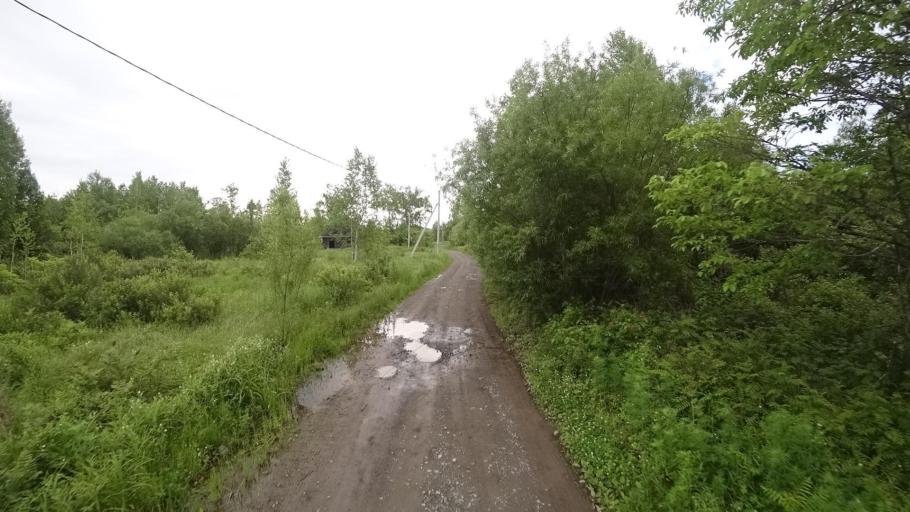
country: RU
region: Khabarovsk Krai
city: Amursk
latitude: 49.9033
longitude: 136.1366
